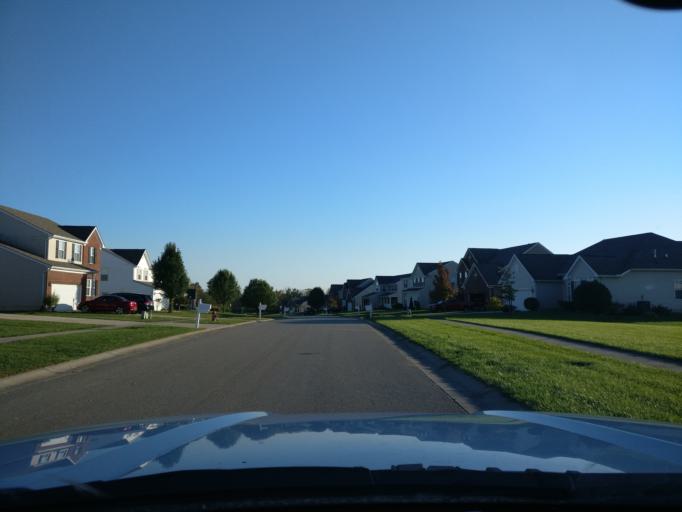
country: US
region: Ohio
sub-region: Warren County
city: Hunter
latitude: 39.4874
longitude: -84.2682
